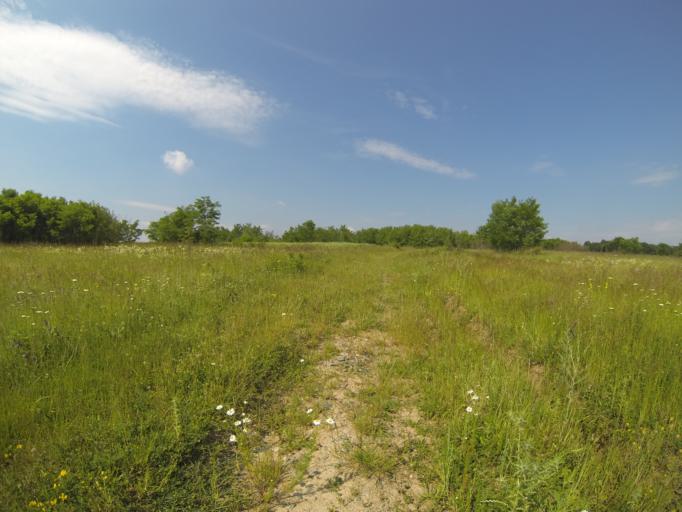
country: RO
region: Gorj
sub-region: Comuna Crusetu
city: Crusetu
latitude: 44.6111
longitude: 23.6625
